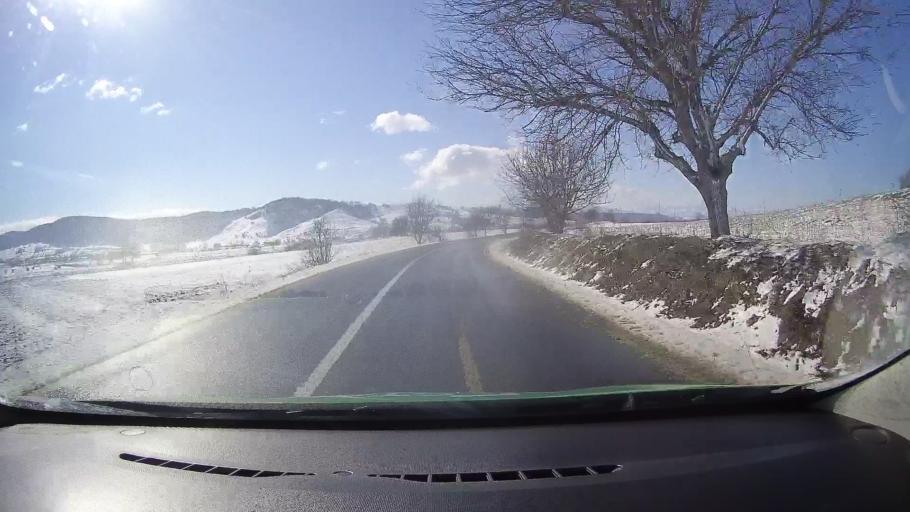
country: RO
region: Sibiu
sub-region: Comuna Rosia
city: Rosia
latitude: 45.7976
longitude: 24.3415
